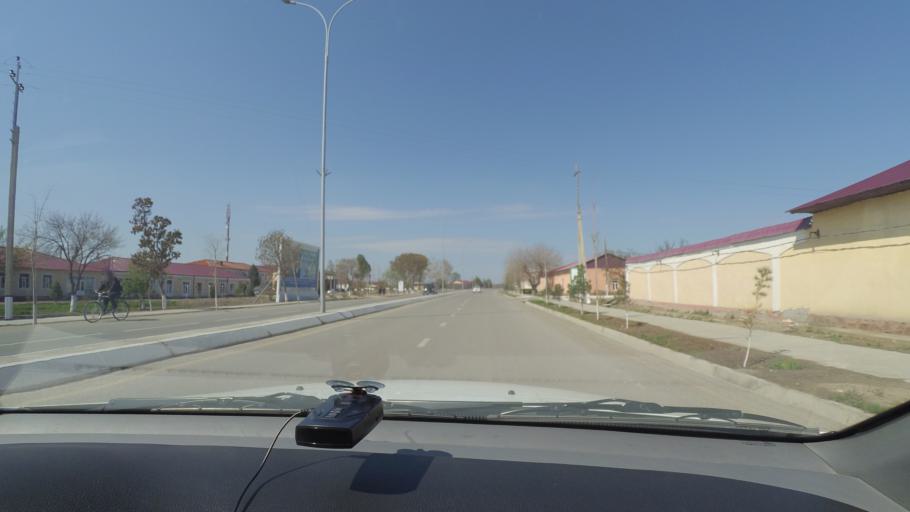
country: UZ
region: Bukhara
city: Kogon
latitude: 39.8003
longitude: 64.5284
